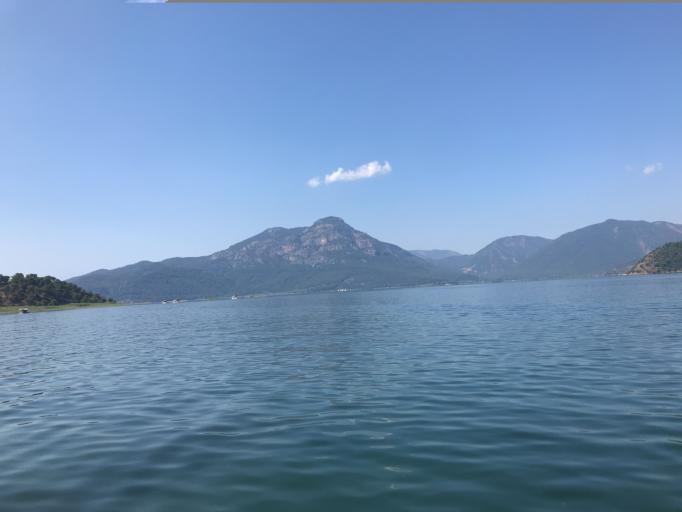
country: TR
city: Dalyan
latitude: 36.9028
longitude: 28.6468
